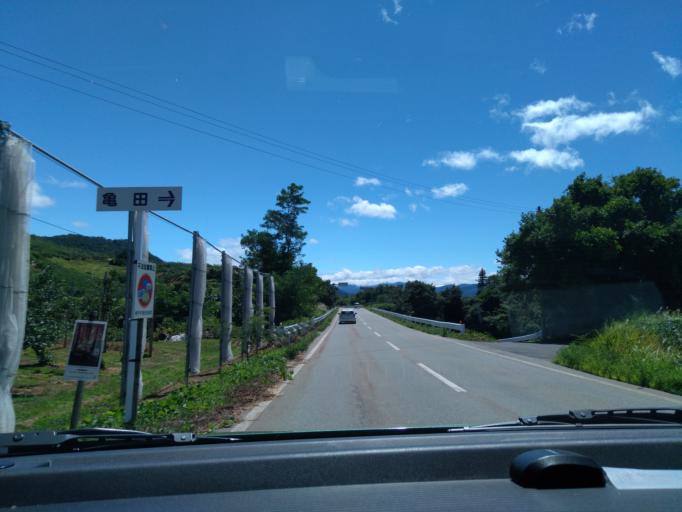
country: JP
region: Akita
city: Yuzawa
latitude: 39.2235
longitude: 140.5654
